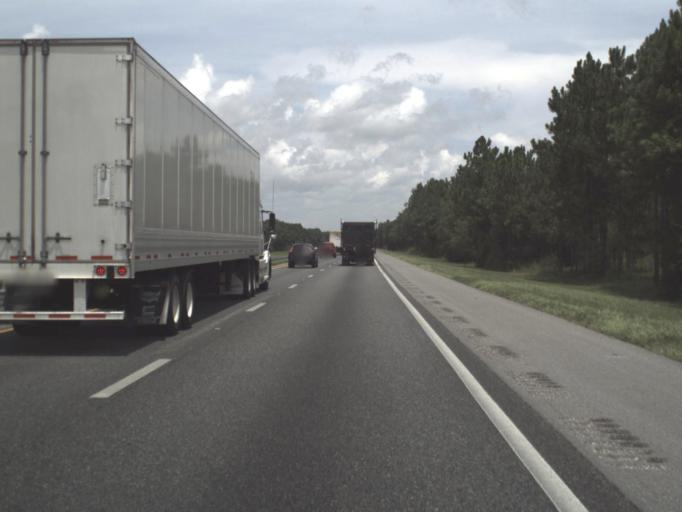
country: US
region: Florida
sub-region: Hernando County
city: Hill 'n Dale
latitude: 28.5463
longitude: -82.2369
